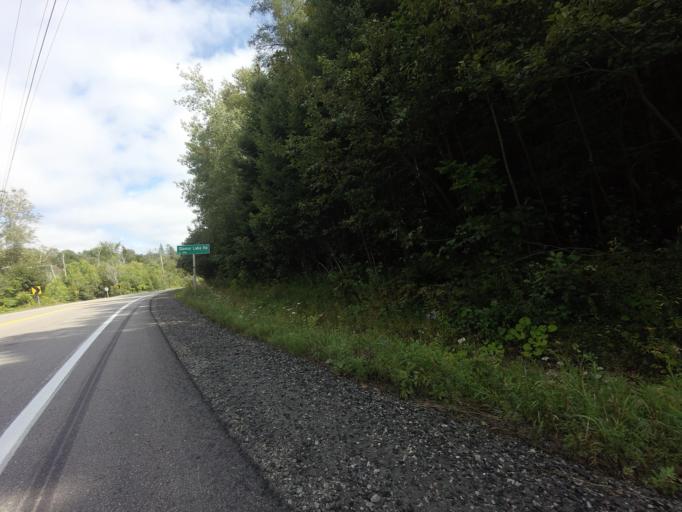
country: CA
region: Ontario
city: Bancroft
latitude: 44.9237
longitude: -78.3414
